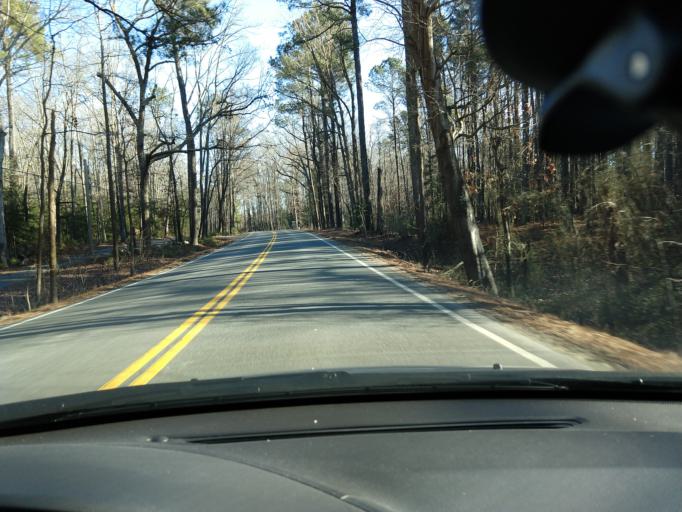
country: US
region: Virginia
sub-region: Surry County
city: Surry
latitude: 37.2634
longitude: -76.8911
